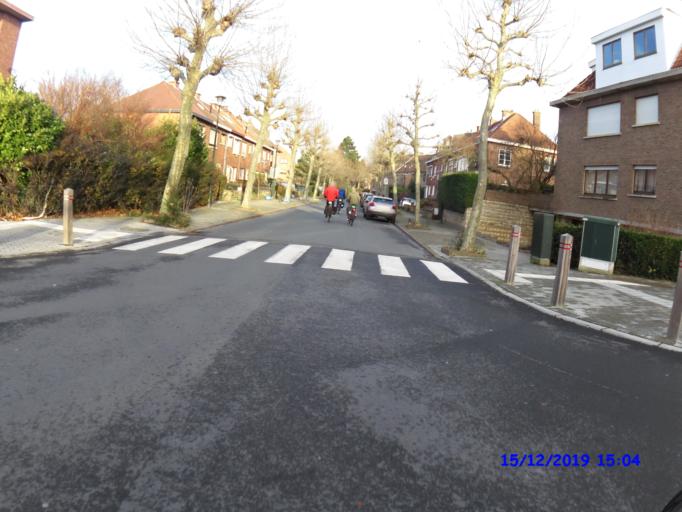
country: BE
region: Flanders
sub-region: Provincie Vlaams-Brabant
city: Drogenbos
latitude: 50.7850
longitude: 4.3252
